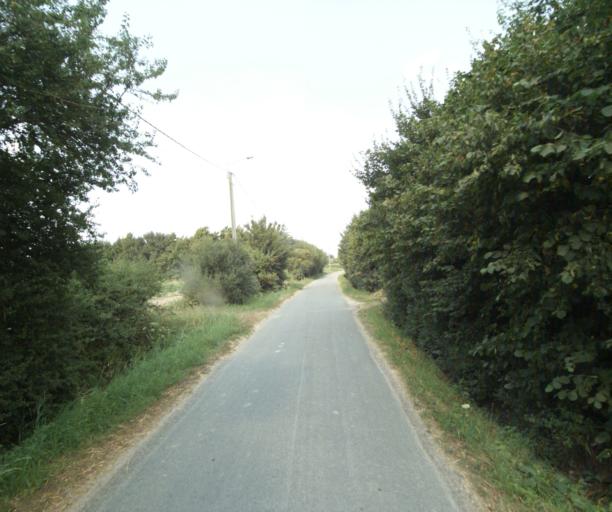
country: FR
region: Nord-Pas-de-Calais
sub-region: Departement du Nord
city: Comines
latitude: 50.7360
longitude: 3.0272
